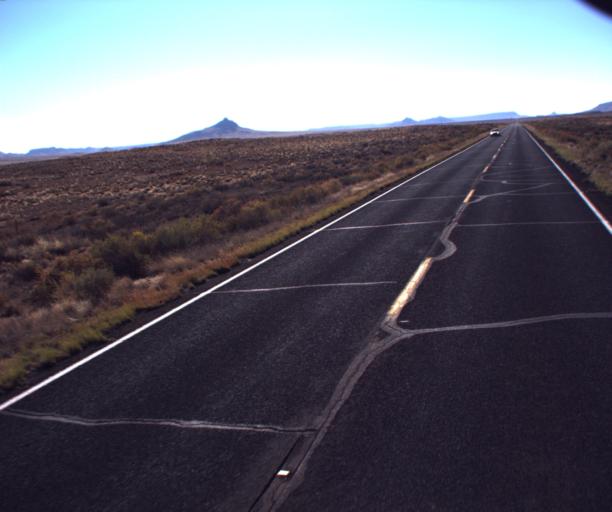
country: US
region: Arizona
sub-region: Navajo County
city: Dilkon
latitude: 35.5911
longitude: -110.4676
